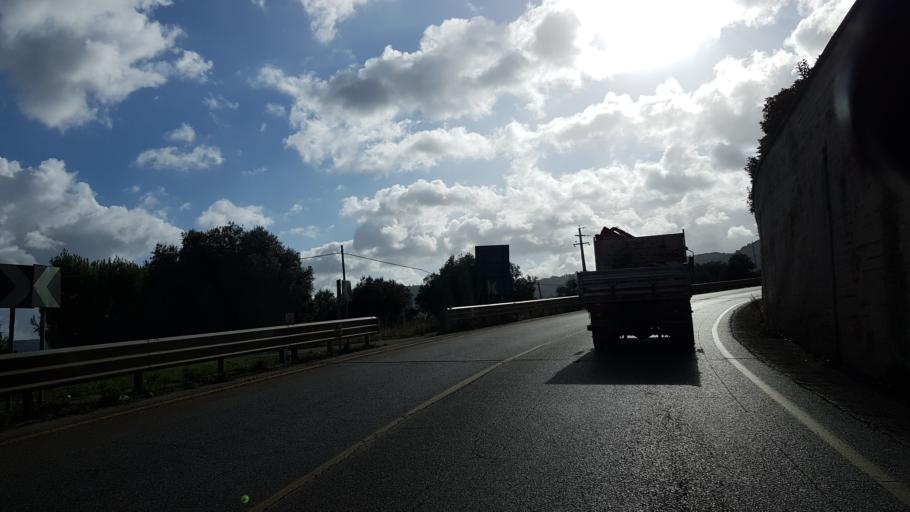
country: IT
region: Apulia
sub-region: Provincia di Brindisi
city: Fasano
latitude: 40.8278
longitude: 17.3508
